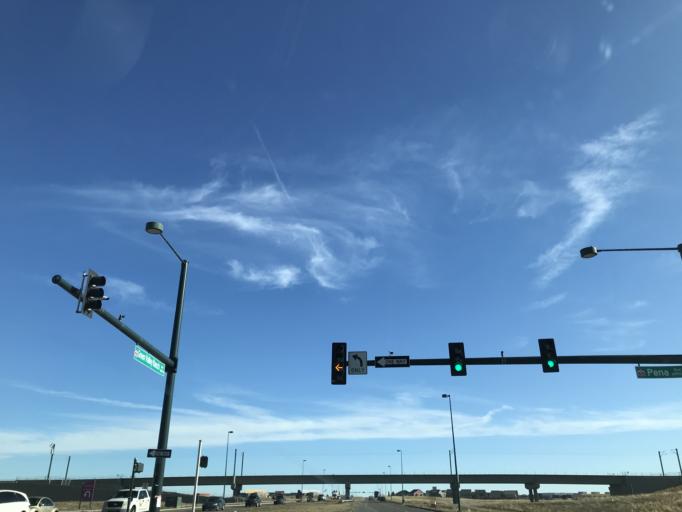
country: US
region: Colorado
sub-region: Adams County
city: Aurora
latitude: 39.7837
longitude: -104.7901
